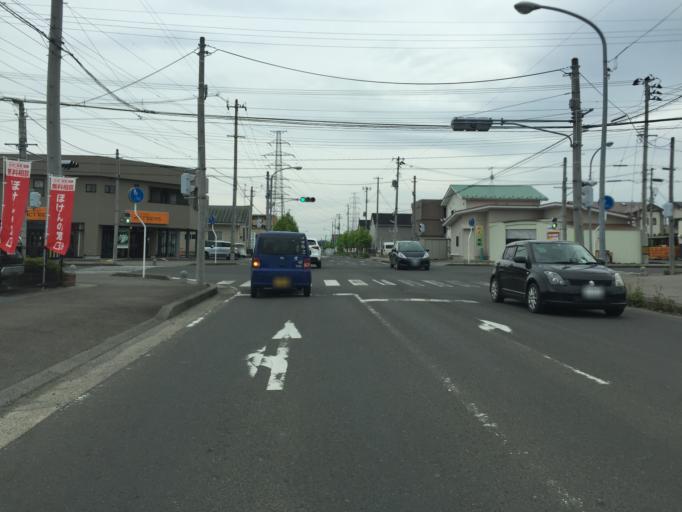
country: JP
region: Fukushima
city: Fukushima-shi
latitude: 37.7900
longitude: 140.4447
